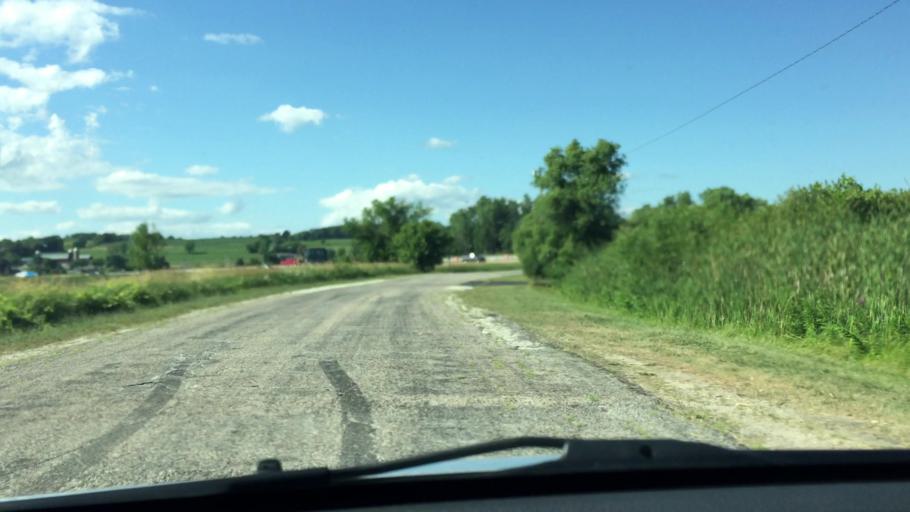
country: US
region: Wisconsin
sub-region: Waukesha County
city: Pewaukee
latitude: 43.0888
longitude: -88.2550
